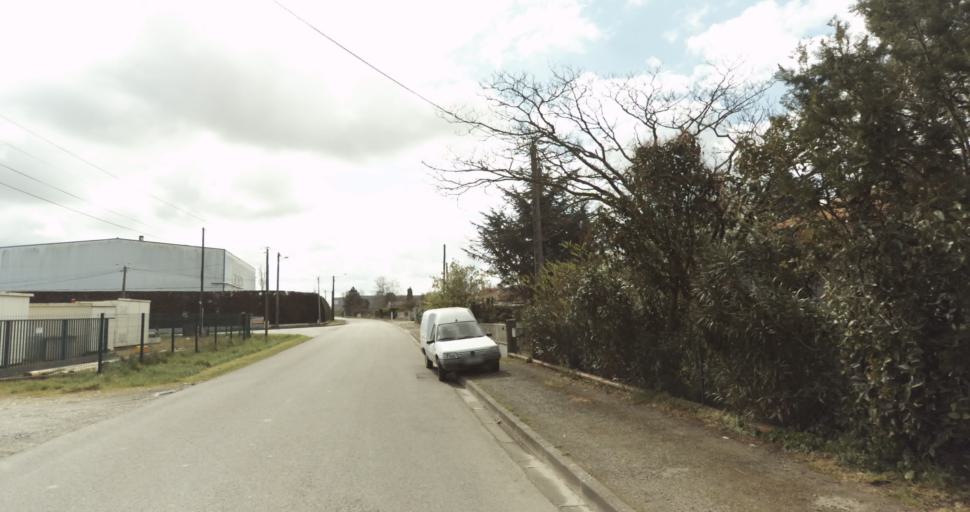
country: FR
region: Midi-Pyrenees
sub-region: Departement de la Haute-Garonne
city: Auterive
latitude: 43.3677
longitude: 1.4613
